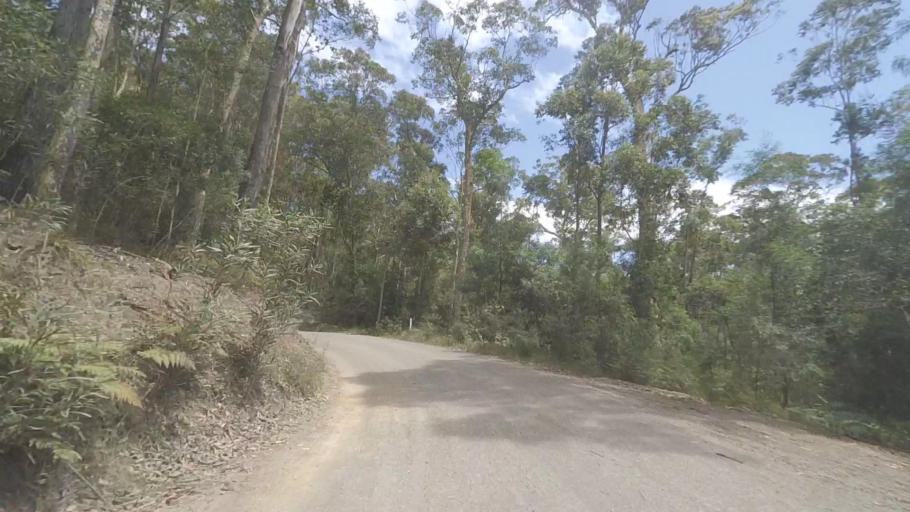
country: AU
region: New South Wales
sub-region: Shoalhaven Shire
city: Milton
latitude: -35.4384
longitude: 150.3213
